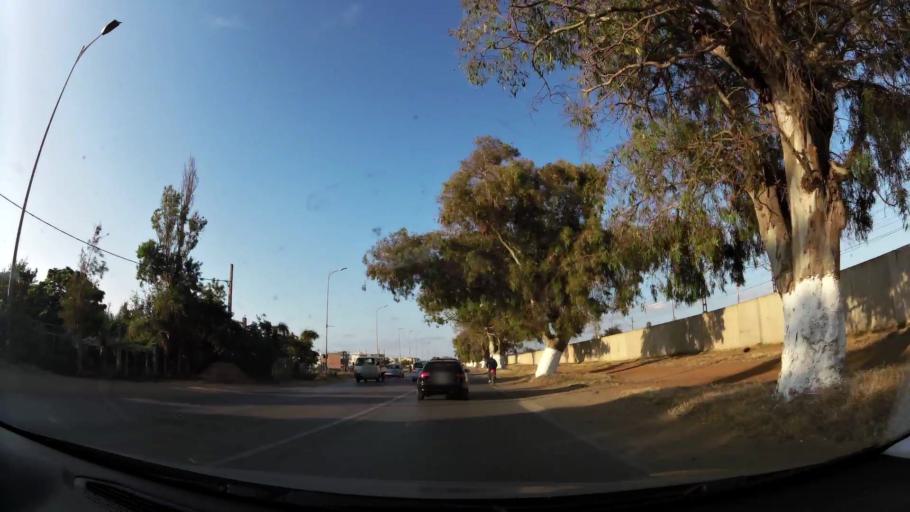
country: MA
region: Rabat-Sale-Zemmour-Zaer
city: Sale
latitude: 34.0839
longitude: -6.7740
